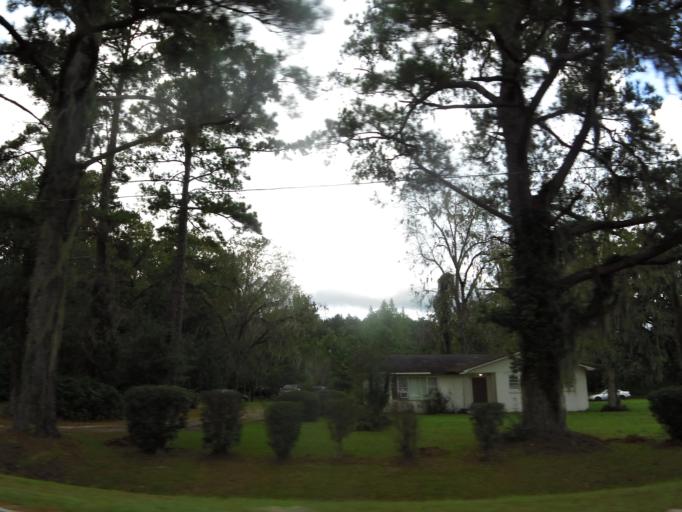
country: US
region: Georgia
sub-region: Liberty County
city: Midway
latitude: 31.8424
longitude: -81.4124
